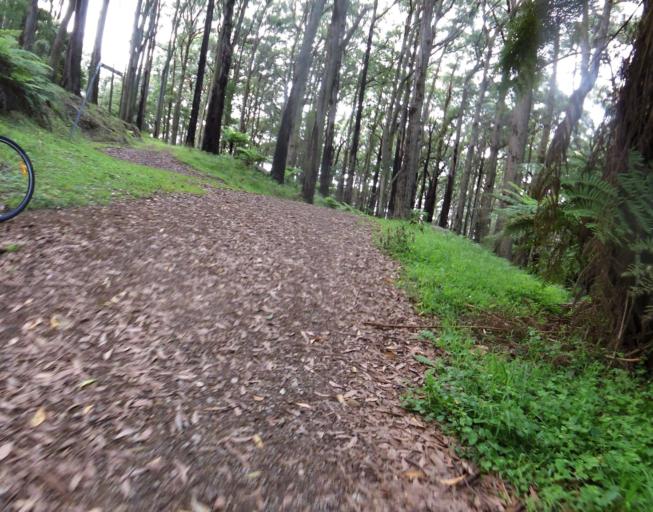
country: AU
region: Victoria
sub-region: Yarra Ranges
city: Mount Dandenong
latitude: -37.8387
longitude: 145.3460
